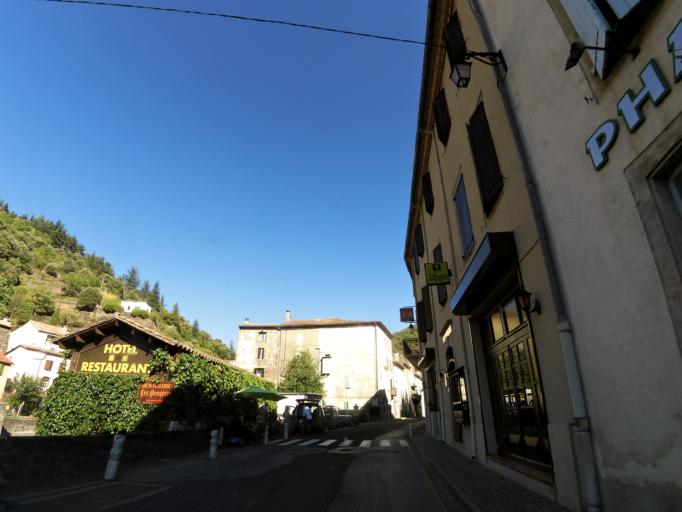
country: FR
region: Languedoc-Roussillon
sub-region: Departement du Gard
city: Valleraugue
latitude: 44.0801
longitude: 3.6434
